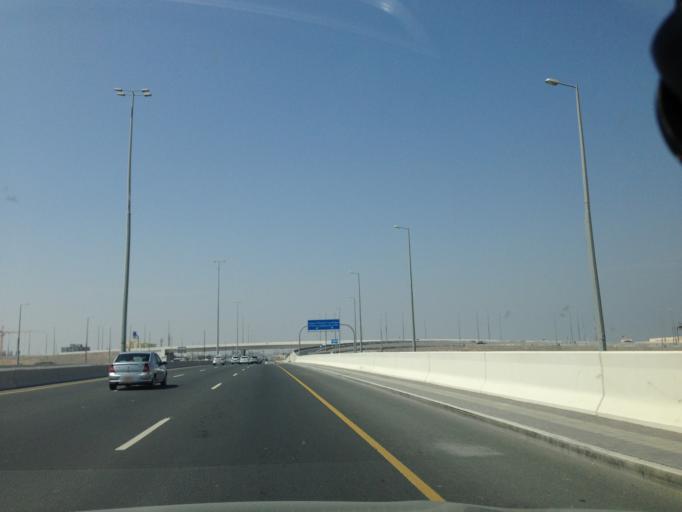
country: OM
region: Muhafazat Masqat
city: As Sib al Jadidah
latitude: 23.6584
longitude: 58.1914
